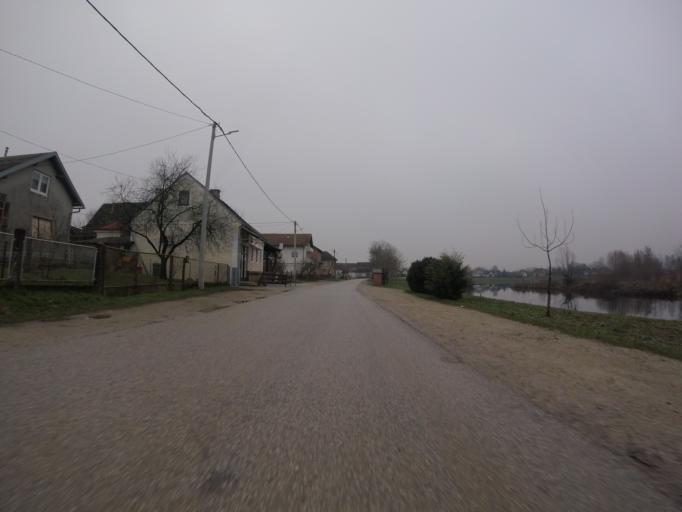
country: HR
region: Sisacko-Moslavacka
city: Lekenik
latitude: 45.6534
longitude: 16.2624
